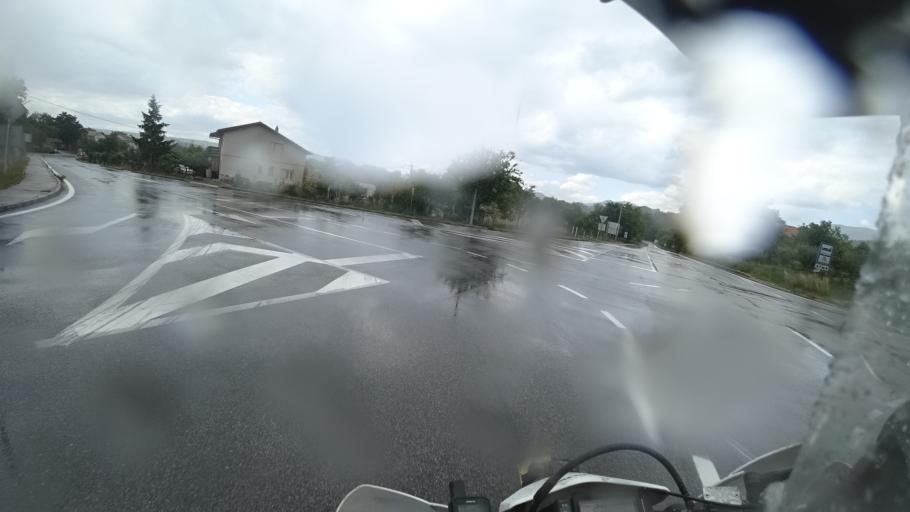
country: HR
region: Sibensko-Kniniska
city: Knin
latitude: 44.0427
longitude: 16.2259
